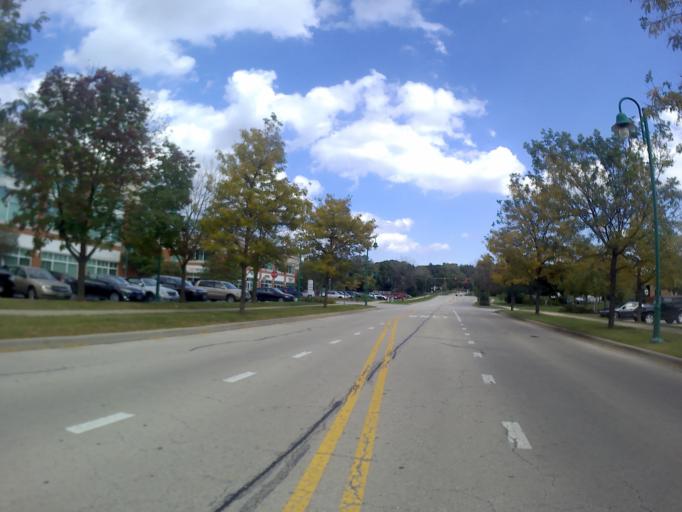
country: US
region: Illinois
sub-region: DuPage County
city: Woodridge
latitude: 41.7662
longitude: -88.0697
